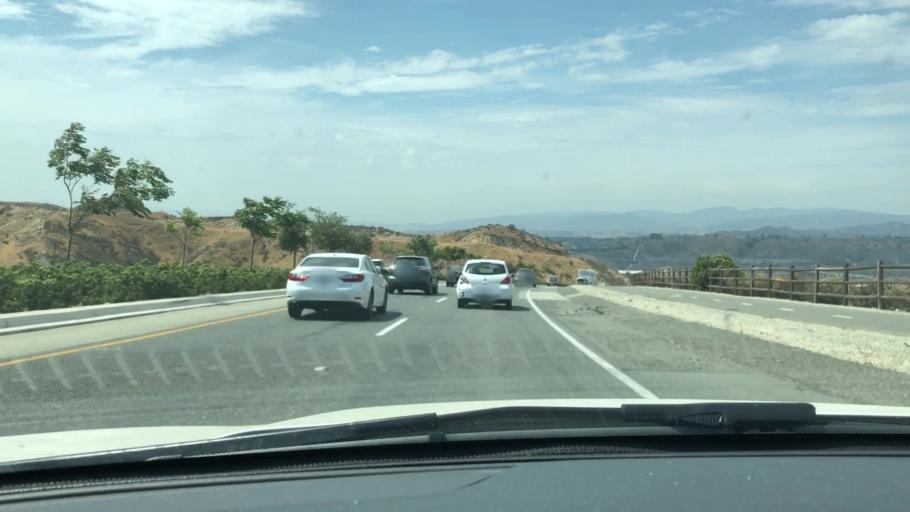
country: US
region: California
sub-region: Los Angeles County
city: Santa Clarita
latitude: 34.4014
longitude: -118.5024
